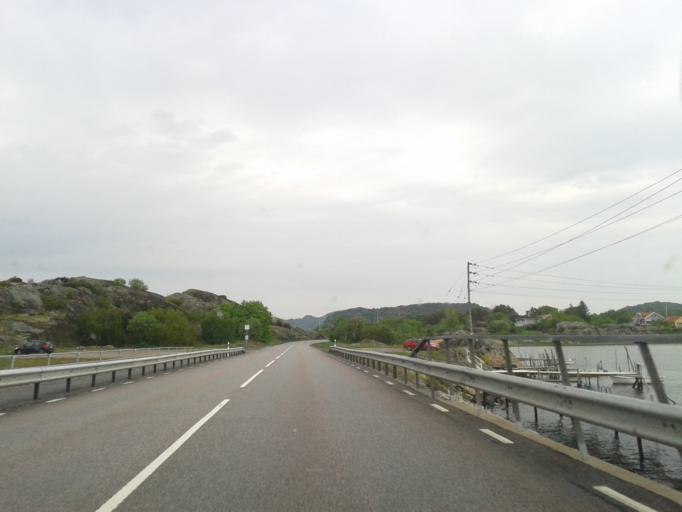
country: SE
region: Vaestra Goetaland
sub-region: Kungalvs Kommun
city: Marstrand
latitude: 57.8919
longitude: 11.7036
